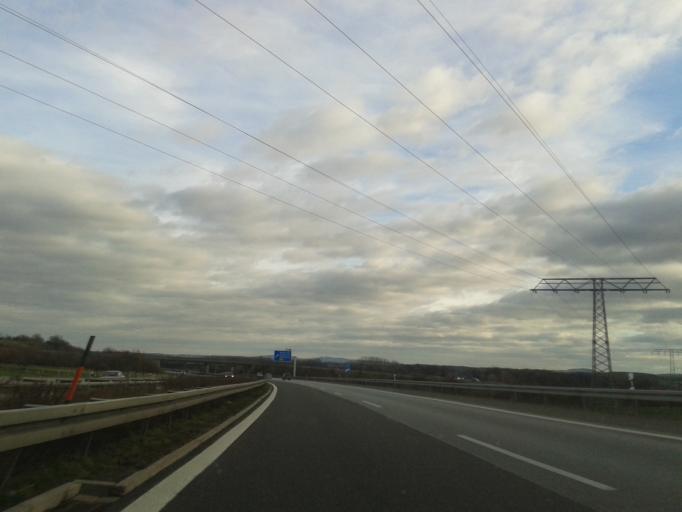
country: DE
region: Saxony
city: Bautzen
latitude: 51.1953
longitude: 14.4601
